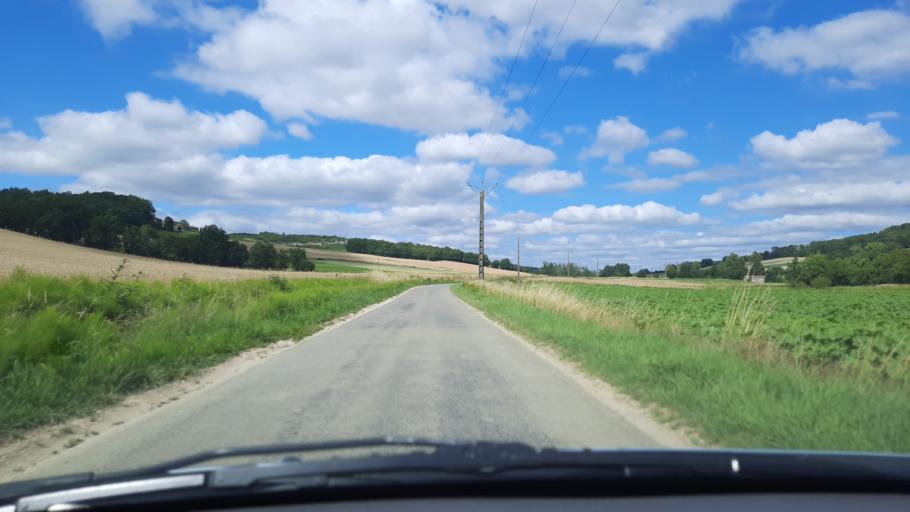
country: FR
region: Midi-Pyrenees
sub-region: Departement du Lot
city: Castelnau-Montratier
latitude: 44.2748
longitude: 1.3969
